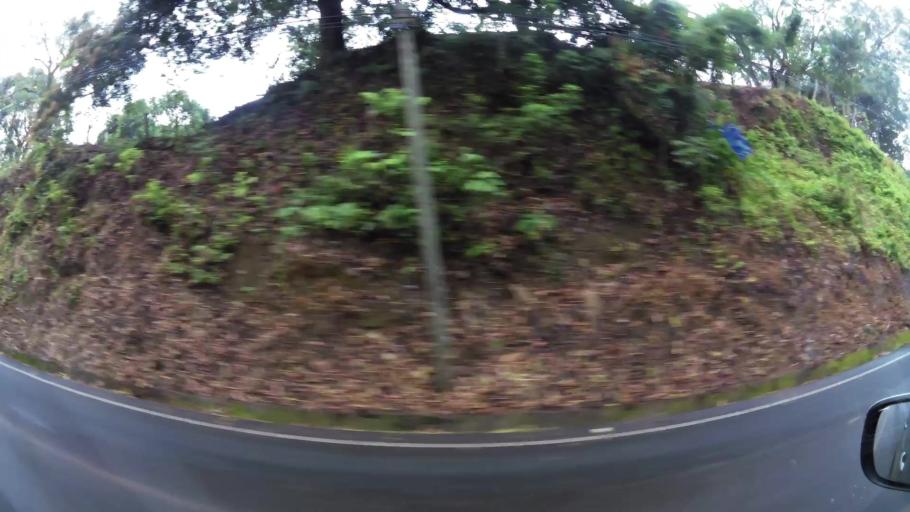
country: CR
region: Alajuela
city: Orotina
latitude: 9.9563
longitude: -84.5762
